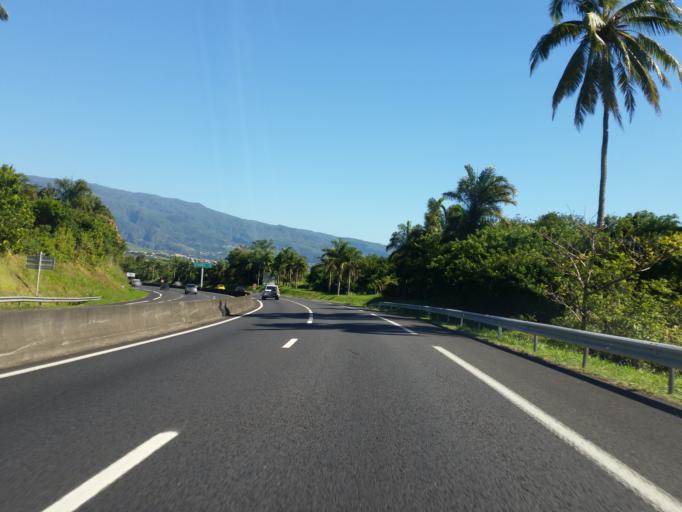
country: RE
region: Reunion
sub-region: Reunion
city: Sainte-Marie
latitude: -20.8981
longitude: 55.5628
